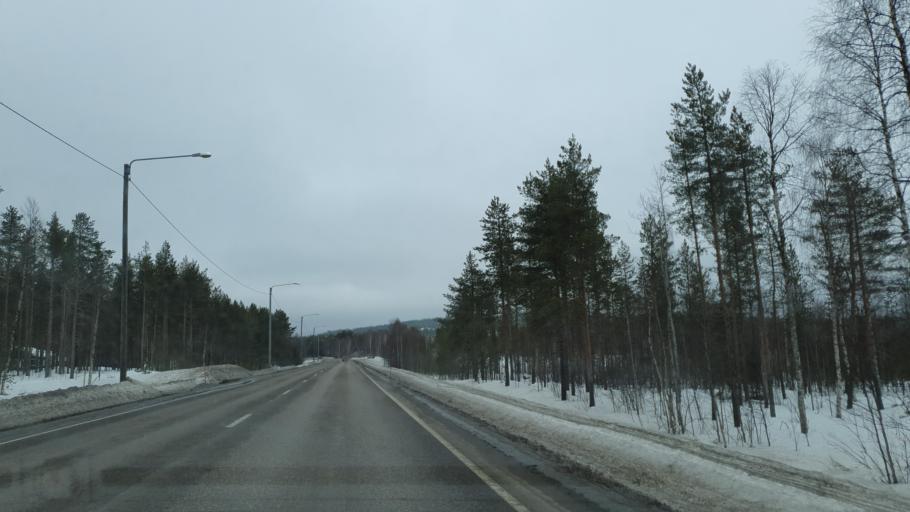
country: FI
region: Lapland
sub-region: Torniolaakso
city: Pello
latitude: 66.9029
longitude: 24.0946
